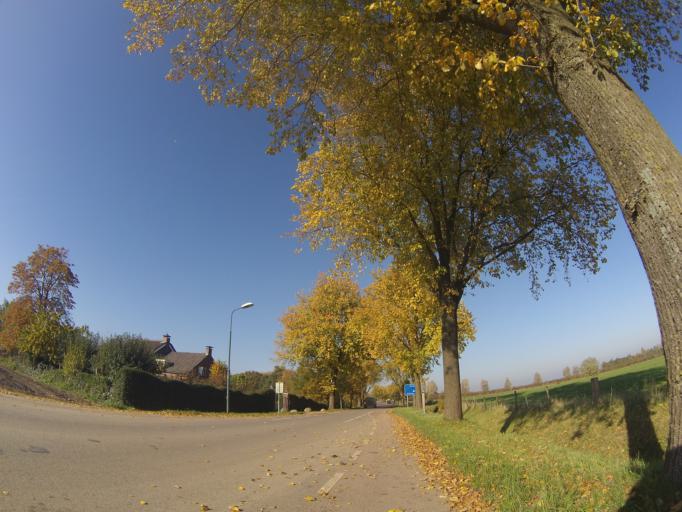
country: NL
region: Utrecht
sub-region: Gemeente Bunnik
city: Bunnik
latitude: 52.0397
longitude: 5.2090
